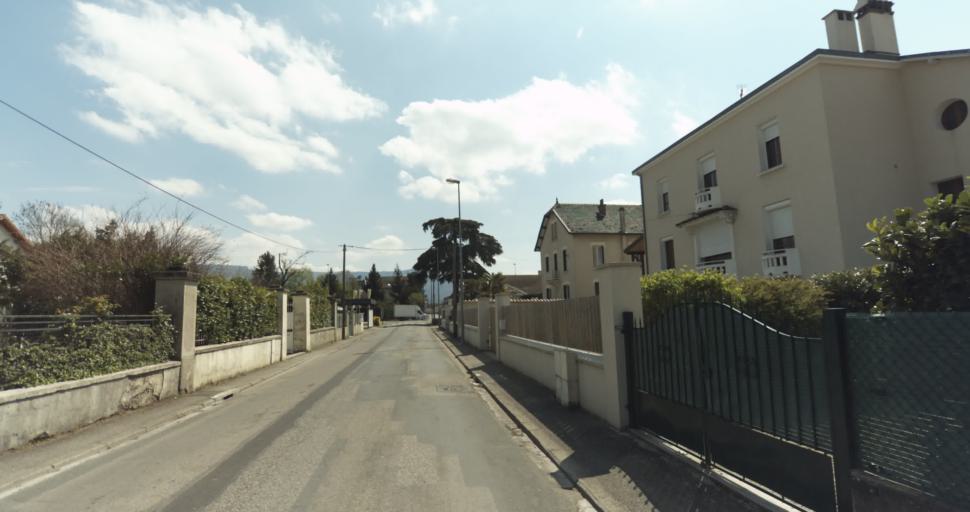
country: FR
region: Rhone-Alpes
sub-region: Departement de l'Isere
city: Saint-Marcellin
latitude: 45.1494
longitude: 5.3128
